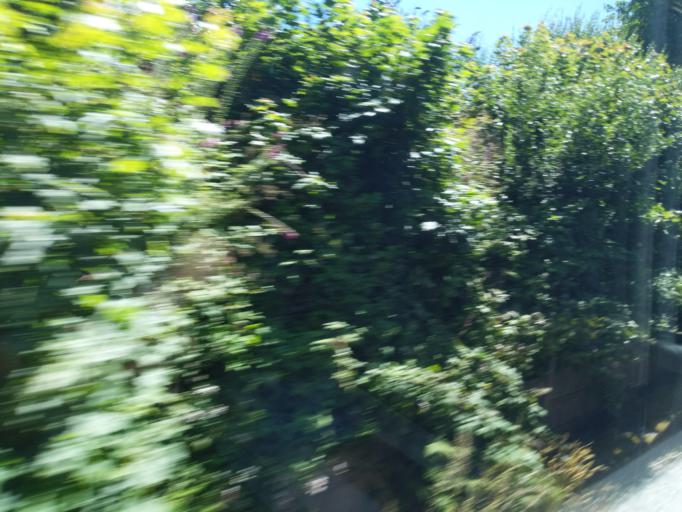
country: GB
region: England
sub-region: Cornwall
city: Redruth
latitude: 50.2501
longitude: -5.2100
